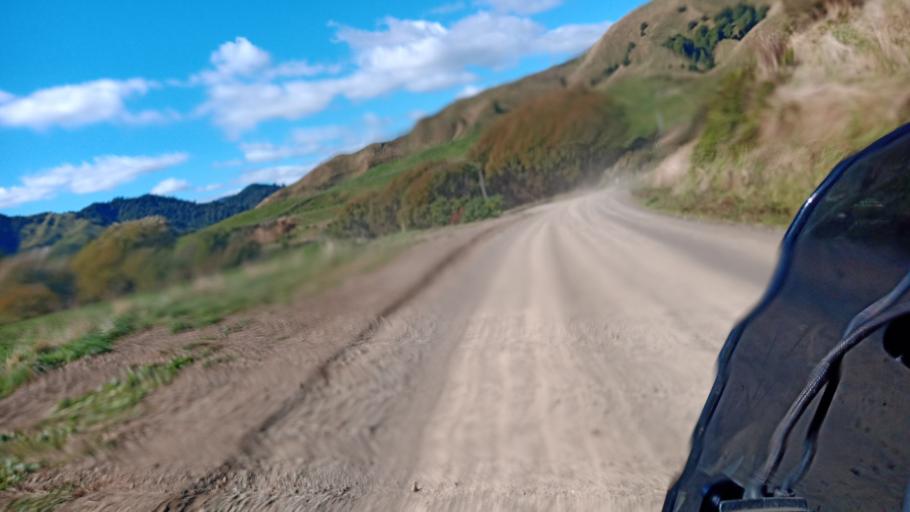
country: NZ
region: Bay of Plenty
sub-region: Opotiki District
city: Opotiki
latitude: -38.2593
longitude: 177.5670
